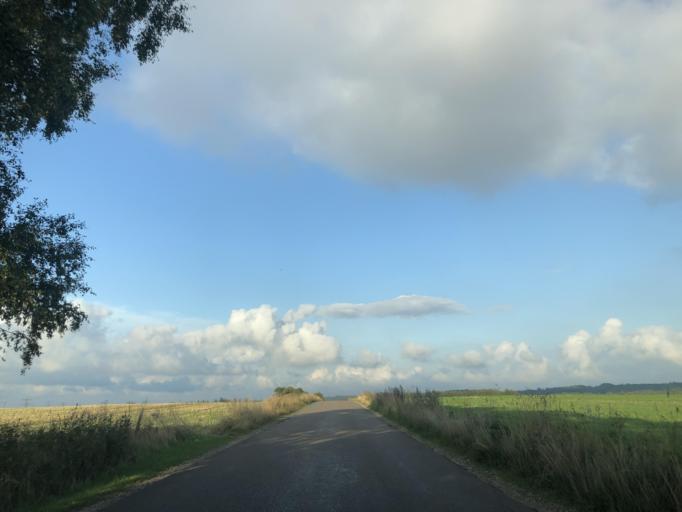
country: DK
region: North Denmark
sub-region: Rebild Kommune
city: Stovring
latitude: 56.9307
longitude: 9.7706
